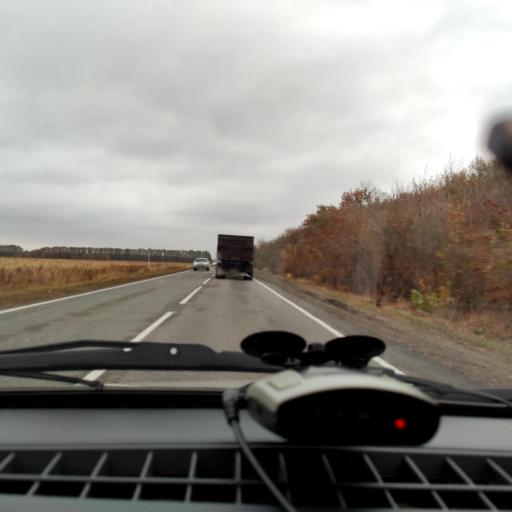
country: RU
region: Voronezj
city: Shilovo
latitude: 51.3911
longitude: 39.0034
